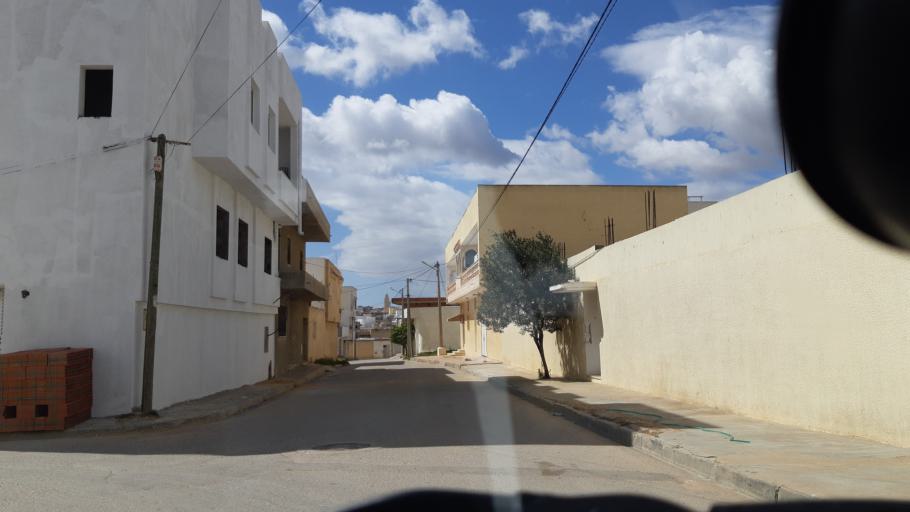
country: TN
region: Susah
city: Akouda
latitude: 35.8784
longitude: 10.5415
